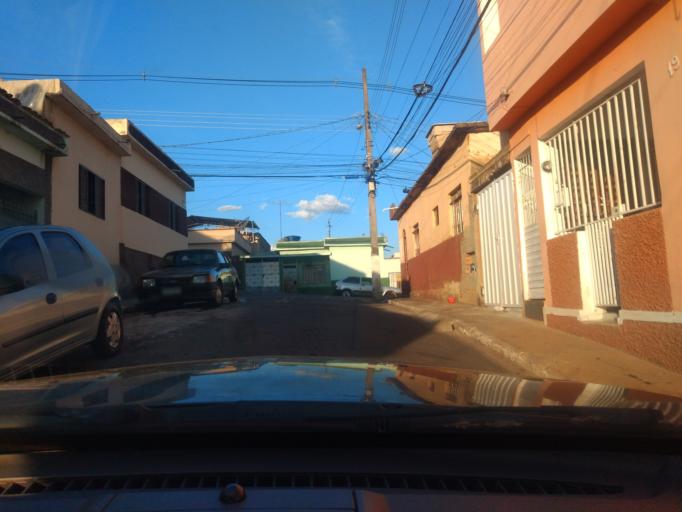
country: BR
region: Minas Gerais
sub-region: Tres Coracoes
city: Tres Coracoes
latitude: -21.6964
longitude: -45.2491
